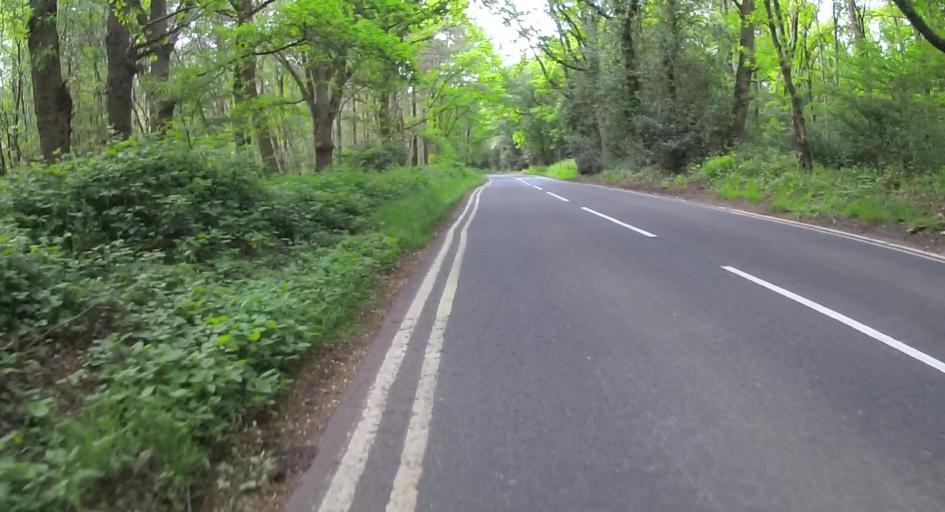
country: GB
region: England
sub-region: Hampshire
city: Fleet
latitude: 51.2875
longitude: -0.7966
